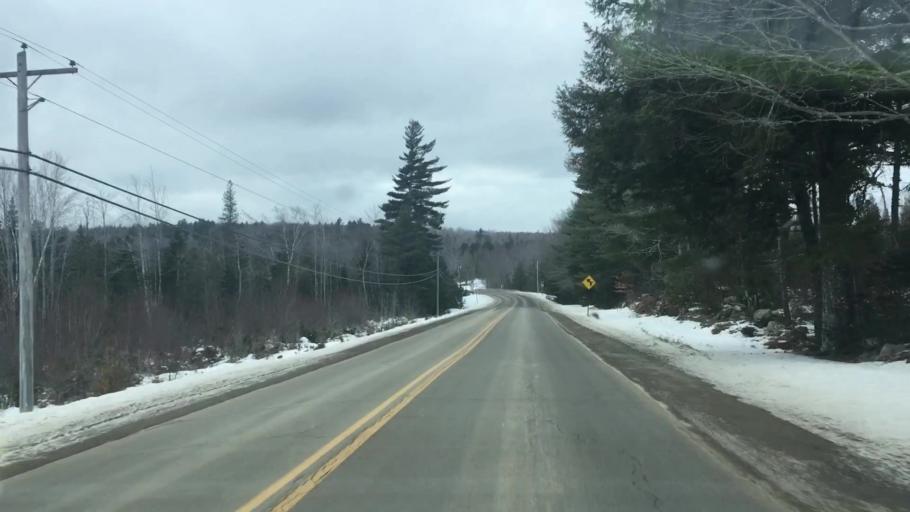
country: US
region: Maine
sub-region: Washington County
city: Calais
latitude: 45.0064
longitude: -67.4129
